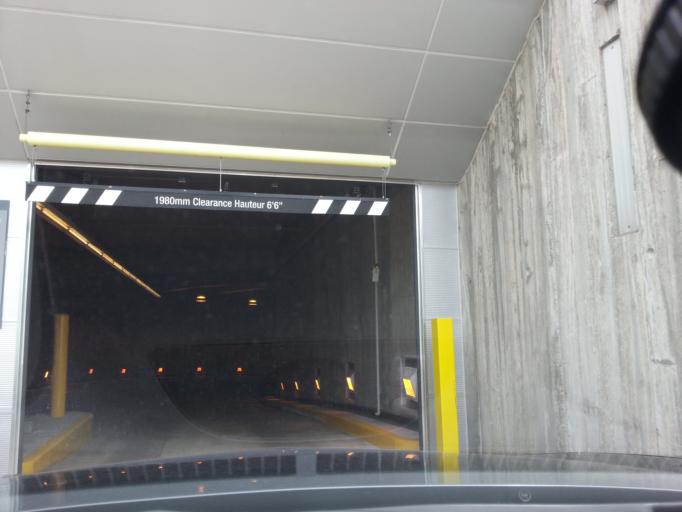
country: CA
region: Ontario
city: Ottawa
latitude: 45.4163
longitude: -75.7184
